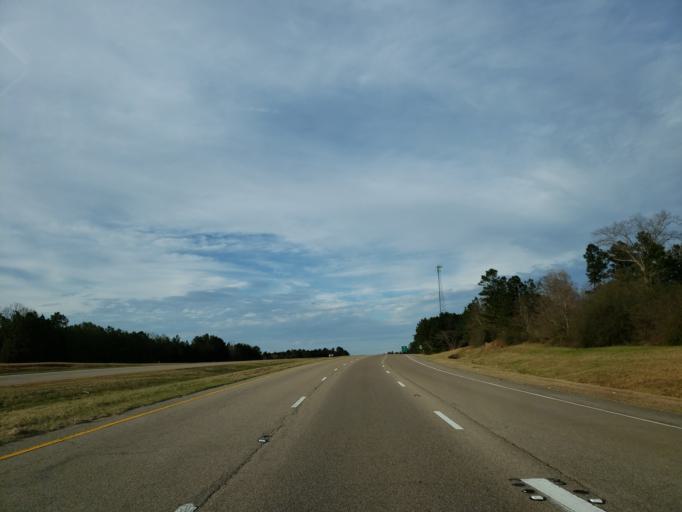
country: US
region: Mississippi
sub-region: Wayne County
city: Waynesboro
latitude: 31.6861
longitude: -88.6171
